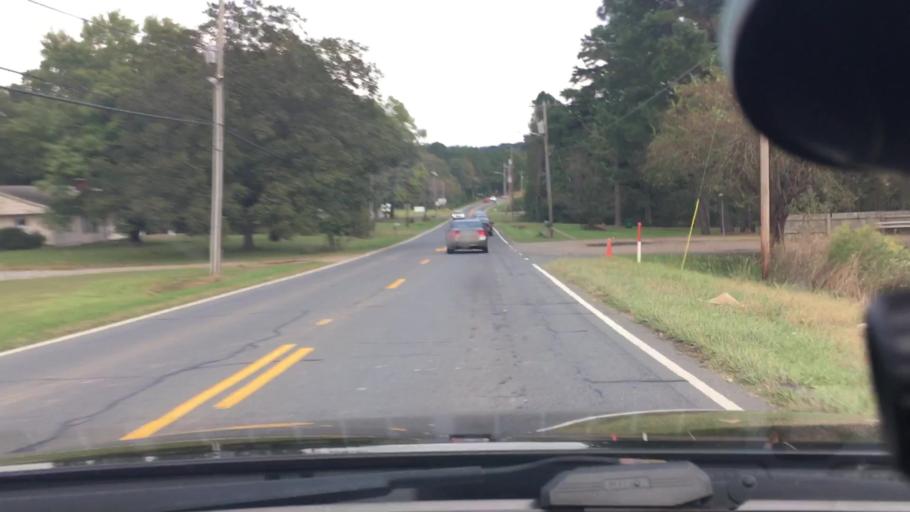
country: US
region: North Carolina
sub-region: Stanly County
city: Albemarle
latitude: 35.3443
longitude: -80.1467
